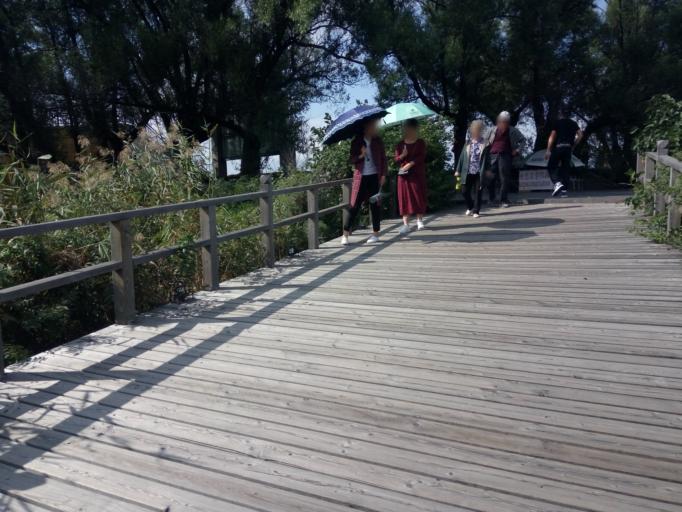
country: CN
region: Heilongjiang Sheng
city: Erjing
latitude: 48.6532
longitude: 126.1469
